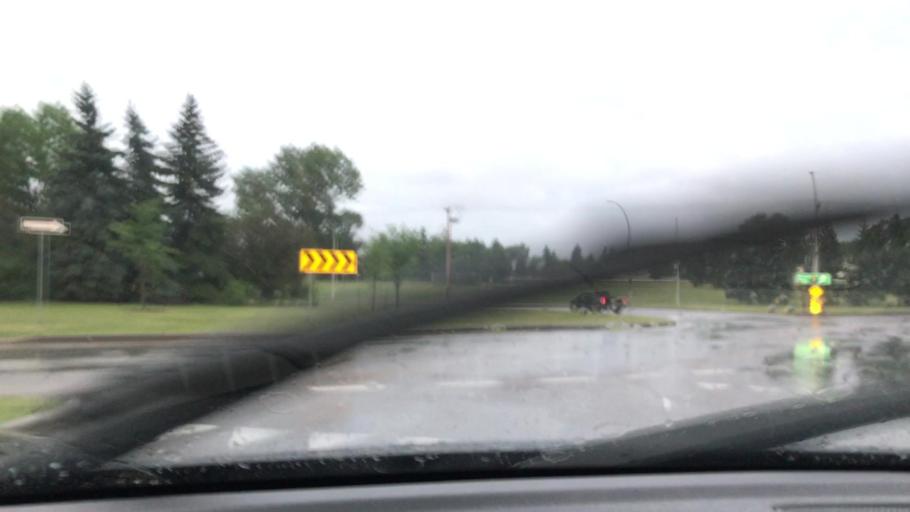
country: CA
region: Alberta
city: Sherwood Park
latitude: 53.5192
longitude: -113.3187
